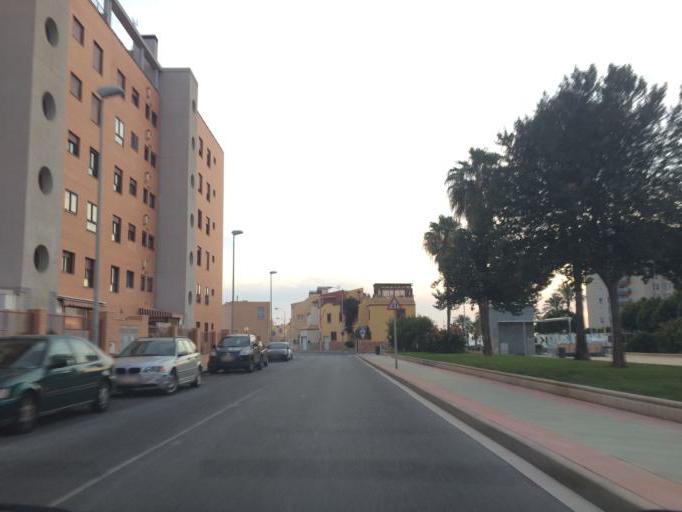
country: ES
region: Andalusia
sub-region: Provincia de Almeria
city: Almeria
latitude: 36.8230
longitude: -2.4401
